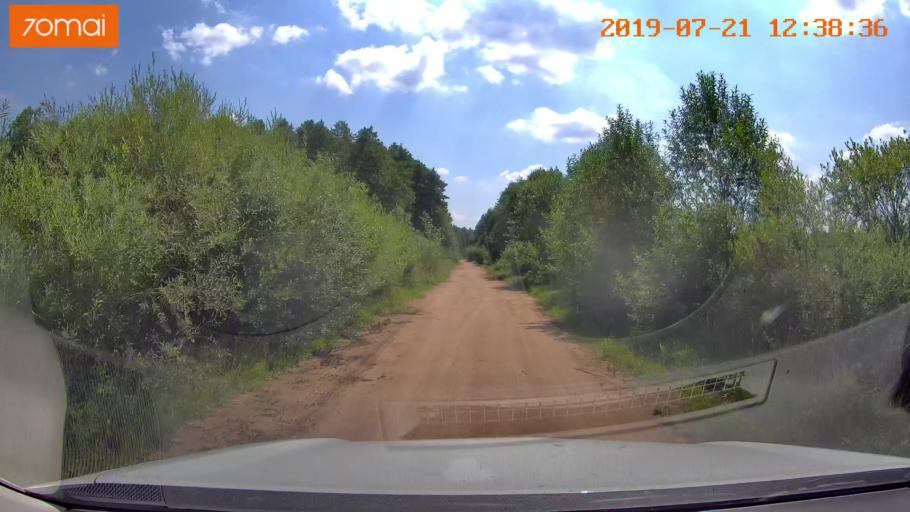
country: BY
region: Grodnenskaya
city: Lyubcha
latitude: 53.8587
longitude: 26.0137
